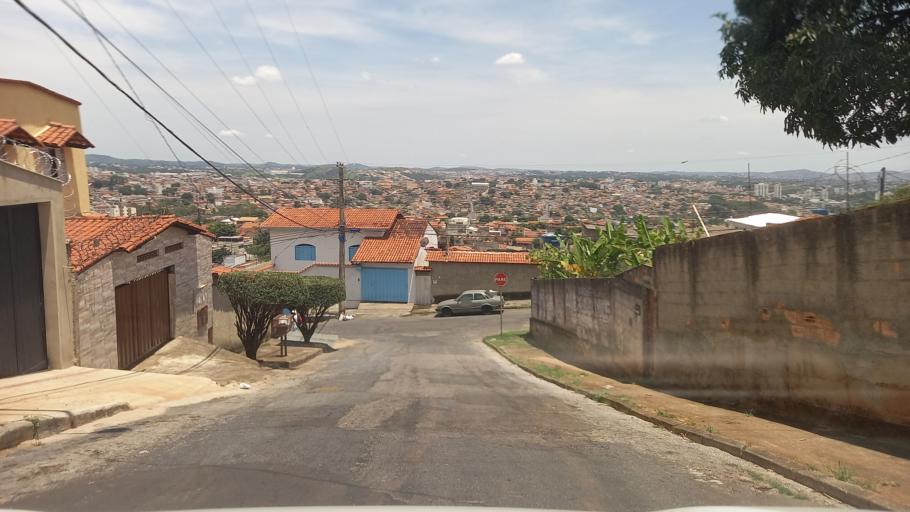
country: BR
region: Minas Gerais
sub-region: Contagem
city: Contagem
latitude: -19.9062
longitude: -44.0130
